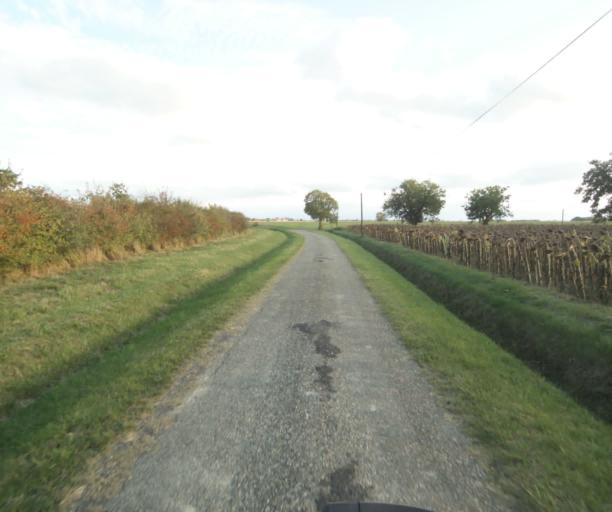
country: FR
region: Midi-Pyrenees
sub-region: Departement du Tarn-et-Garonne
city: Verdun-sur-Garonne
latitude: 43.8359
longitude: 1.1697
